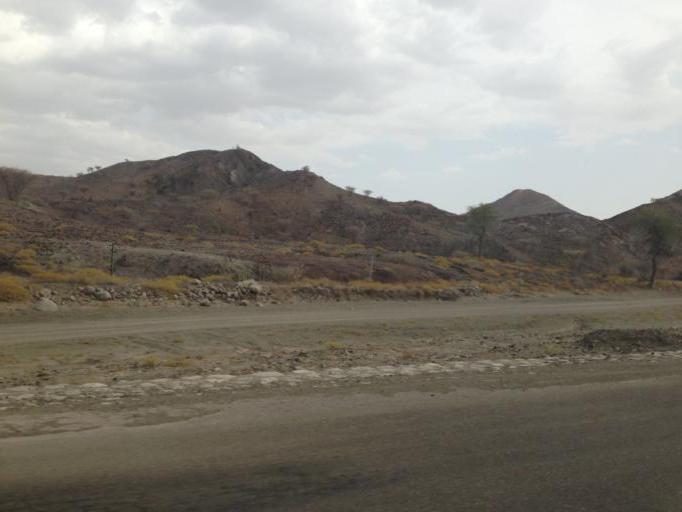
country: OM
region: Ash Sharqiyah
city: Badiyah
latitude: 22.5535
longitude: 59.0046
